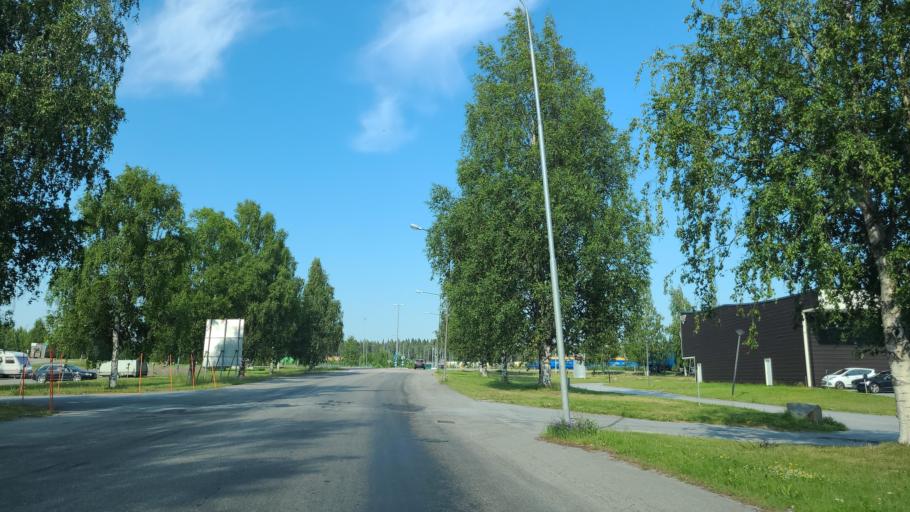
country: SE
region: Vaesterbotten
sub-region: Umea Kommun
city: Umea
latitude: 63.8450
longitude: 20.2278
